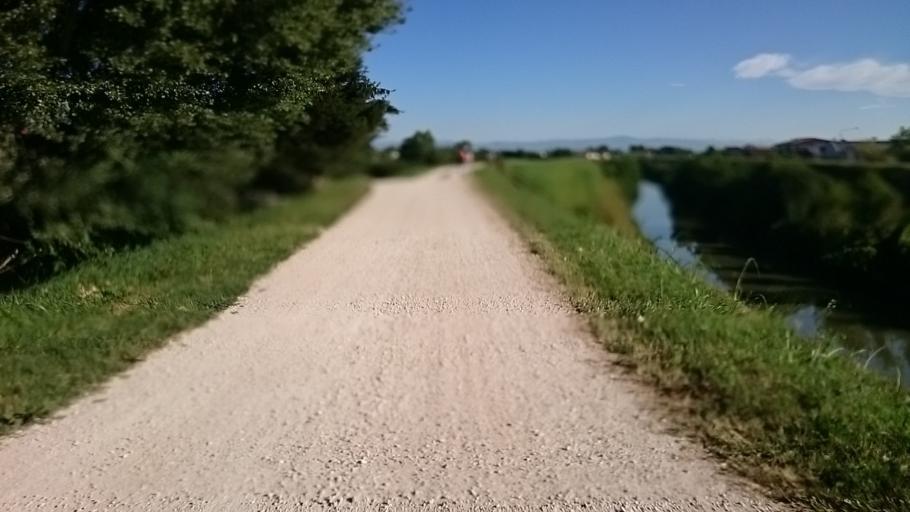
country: IT
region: Veneto
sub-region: Provincia di Padova
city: Vigodarzere
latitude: 45.4605
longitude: 11.8945
